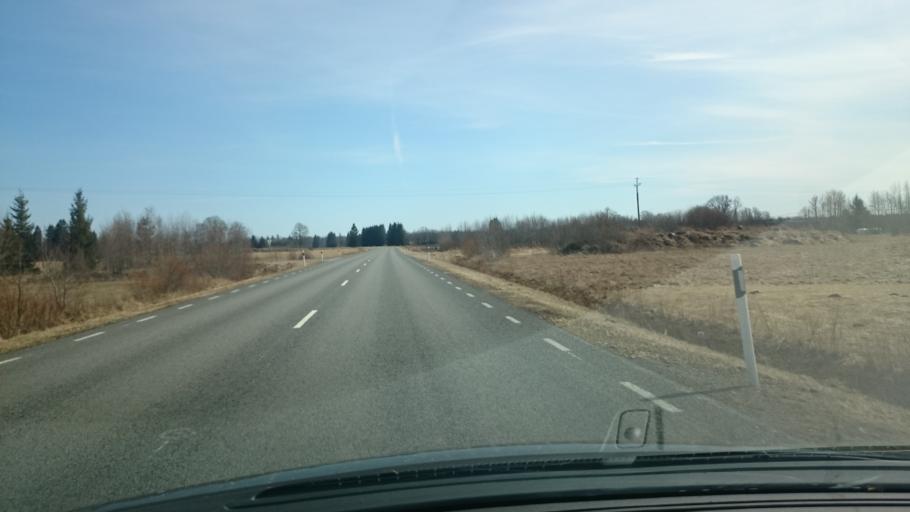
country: EE
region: Paernumaa
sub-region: Tootsi vald
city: Tootsi
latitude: 58.6676
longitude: 24.7779
